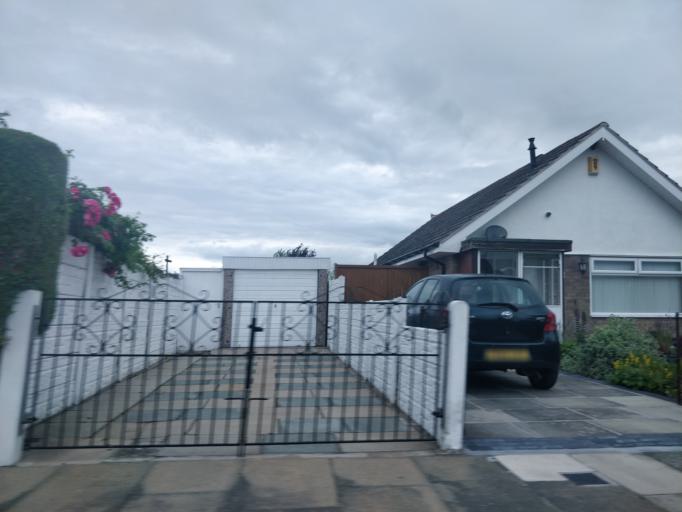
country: GB
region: England
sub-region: Sefton
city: Southport
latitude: 53.6728
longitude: -2.9689
